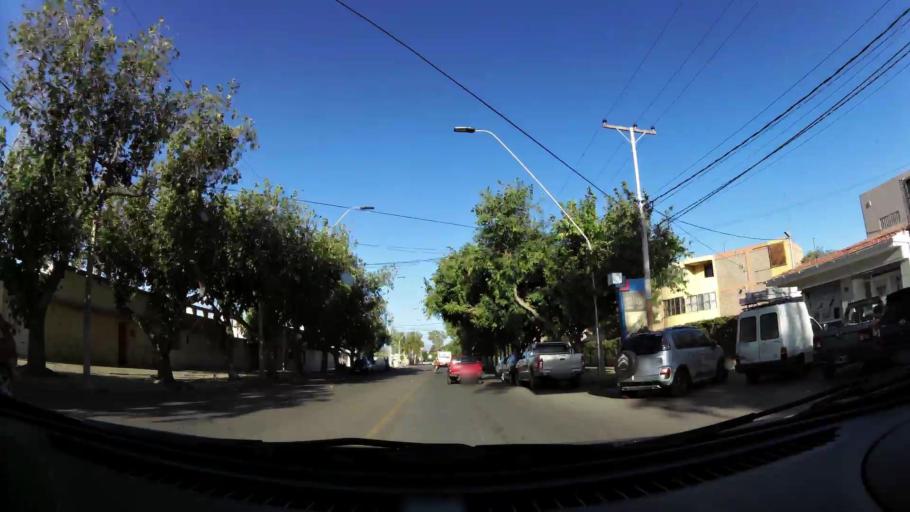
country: AR
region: San Juan
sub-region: Departamento de Santa Lucia
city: Santa Lucia
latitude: -31.5336
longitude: -68.5102
